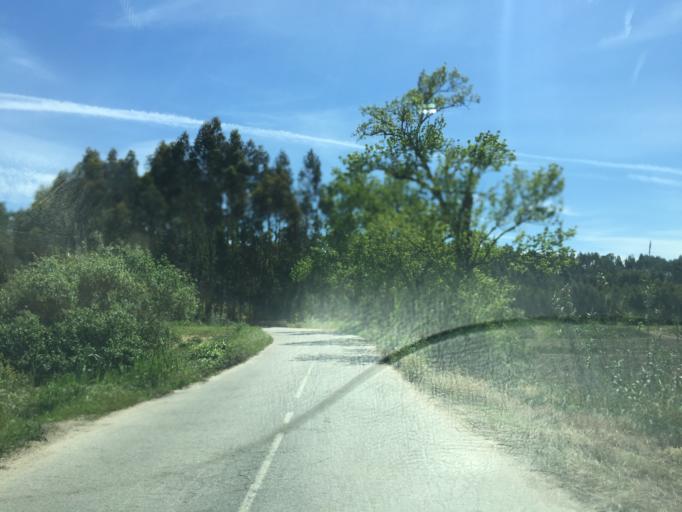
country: PT
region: Leiria
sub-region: Pombal
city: Lourical
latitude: 40.0666
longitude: -8.7573
